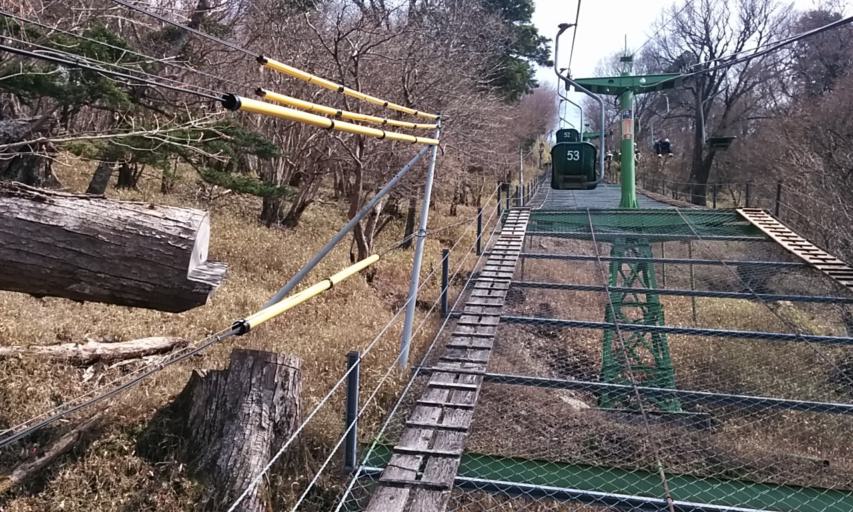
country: JP
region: Tokushima
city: Wakimachi
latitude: 33.8647
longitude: 134.0900
